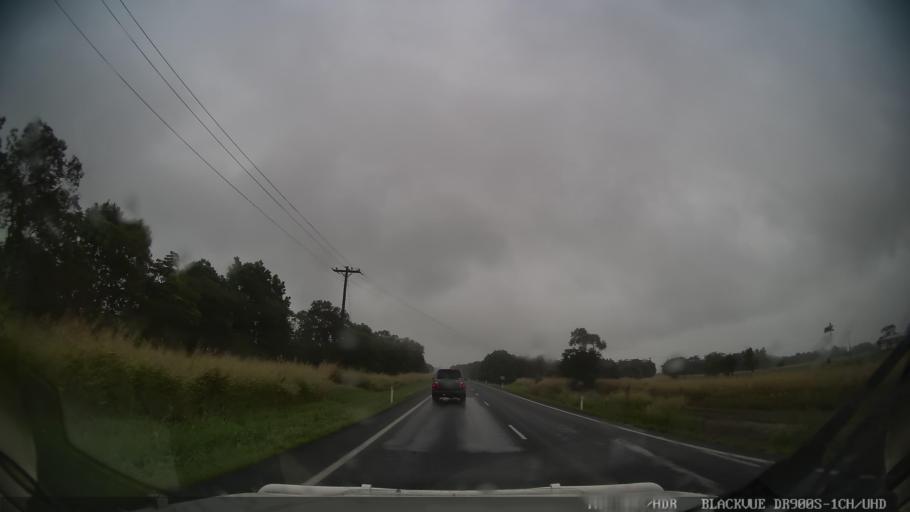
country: AU
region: Queensland
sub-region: Cassowary Coast
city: Innisfail
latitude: -17.6526
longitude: 146.0344
